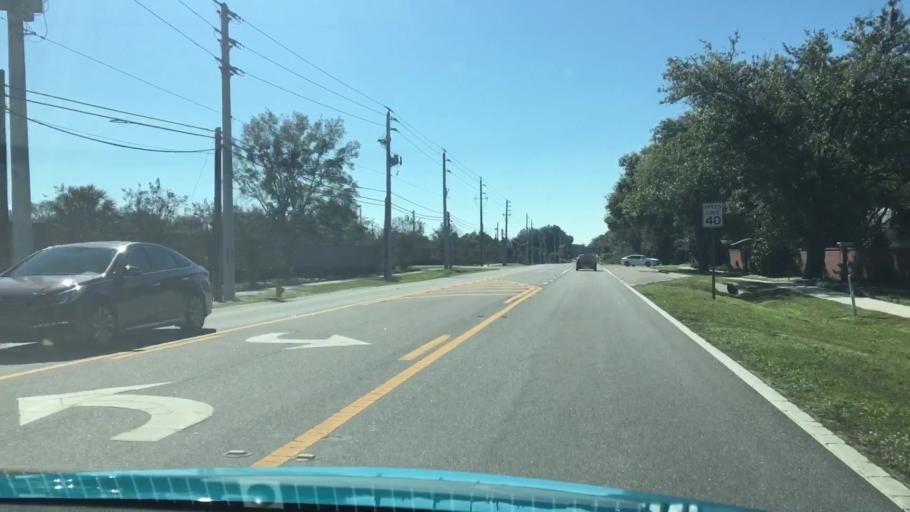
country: US
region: Florida
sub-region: Seminole County
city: Heathrow
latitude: 28.7974
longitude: -81.3630
